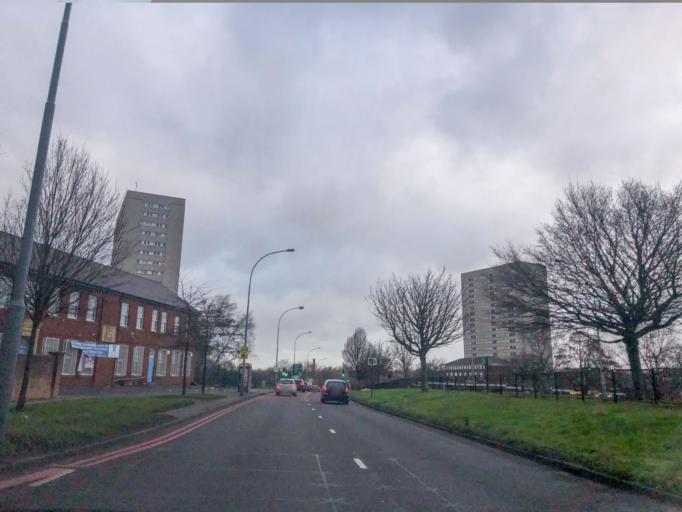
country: GB
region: England
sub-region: City and Borough of Birmingham
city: Hockley
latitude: 52.4828
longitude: -1.9229
